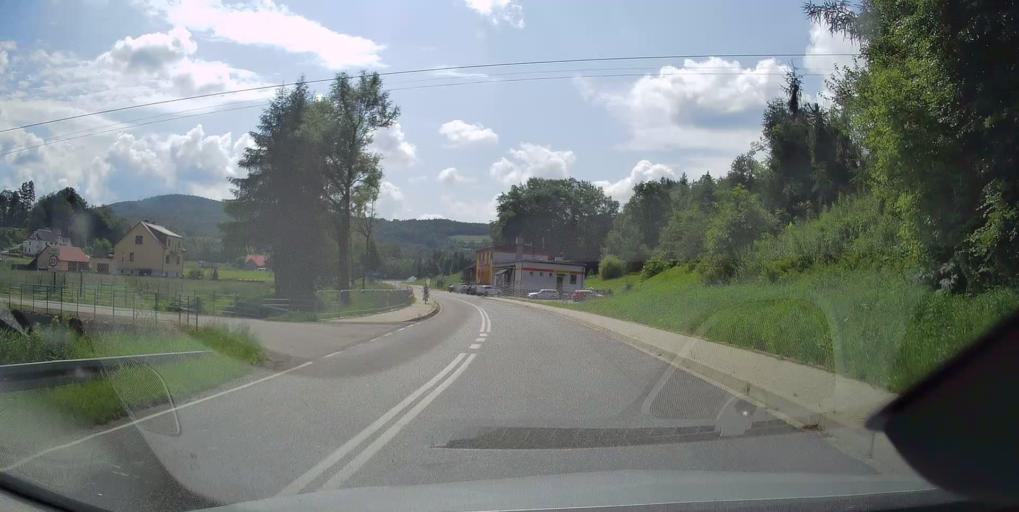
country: PL
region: Lesser Poland Voivodeship
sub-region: Powiat tarnowski
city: Zakliczyn
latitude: 49.7986
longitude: 20.7972
